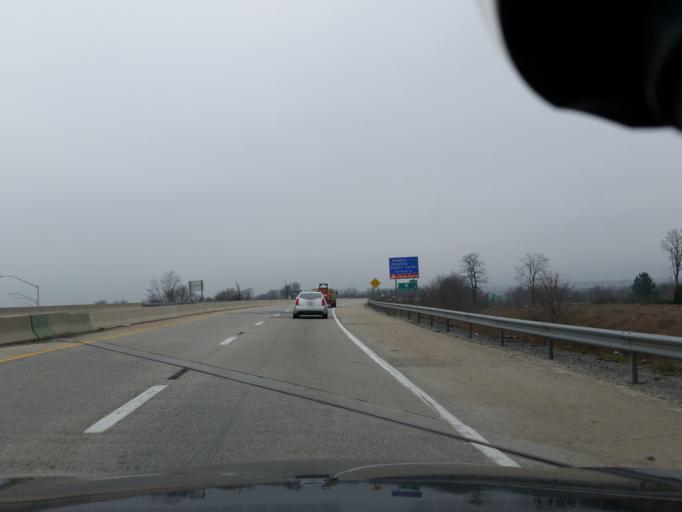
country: US
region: Pennsylvania
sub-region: Cumberland County
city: Shiremanstown
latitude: 40.2377
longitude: -76.9765
